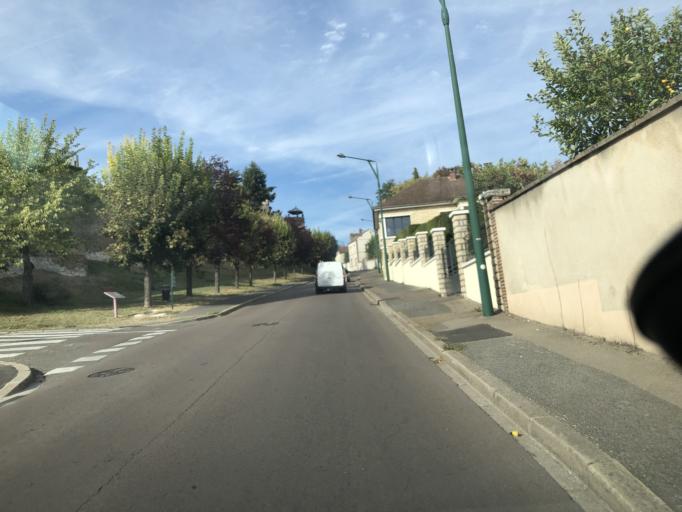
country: FR
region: Bourgogne
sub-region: Departement de l'Yonne
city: Joigny
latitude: 47.9809
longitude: 3.4012
